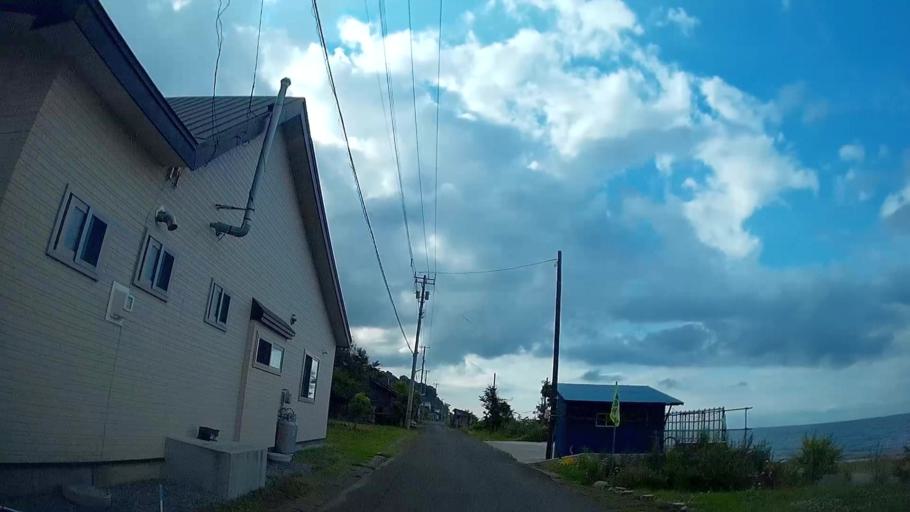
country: JP
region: Hokkaido
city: Nanae
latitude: 42.1160
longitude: 140.5427
